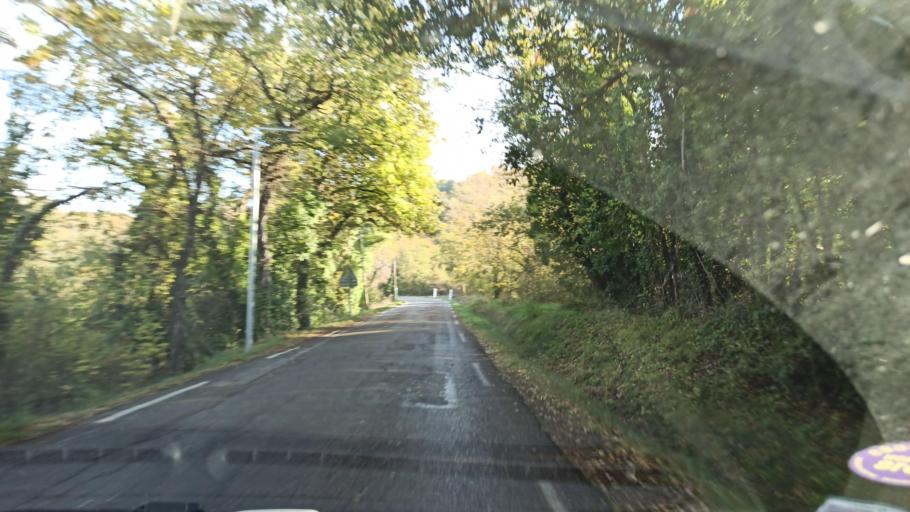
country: FR
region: Provence-Alpes-Cote d'Azur
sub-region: Departement du Vaucluse
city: Goult
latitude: 43.8372
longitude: 5.2656
